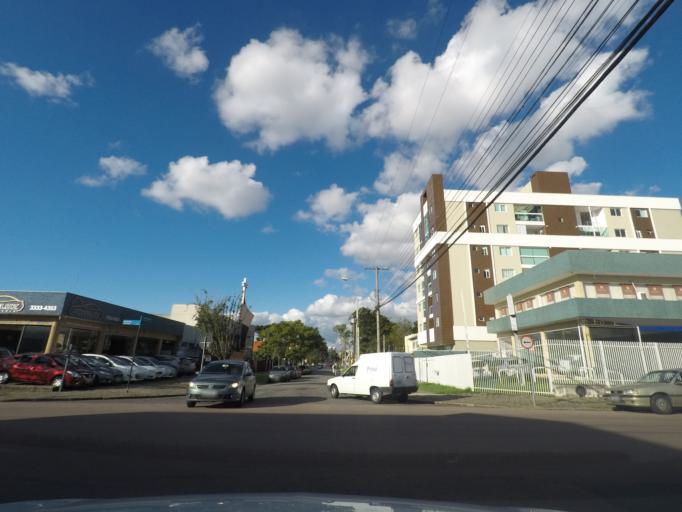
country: BR
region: Parana
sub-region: Curitiba
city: Curitiba
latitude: -25.4483
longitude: -49.2680
